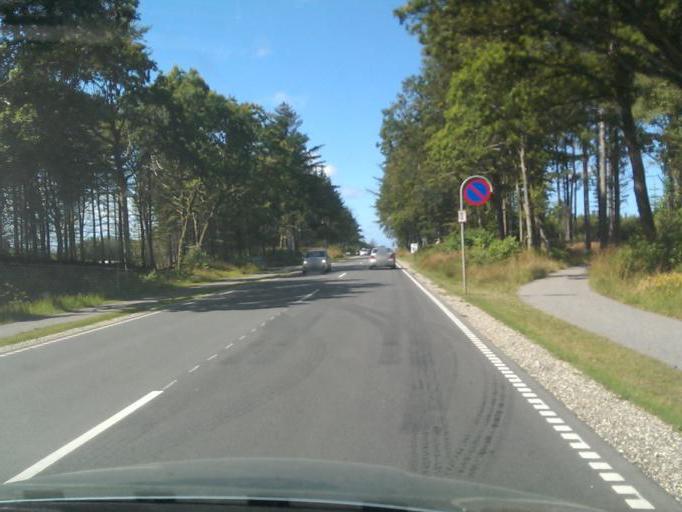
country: DK
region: North Denmark
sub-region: Jammerbugt Kommune
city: Pandrup
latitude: 57.2497
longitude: 9.6040
